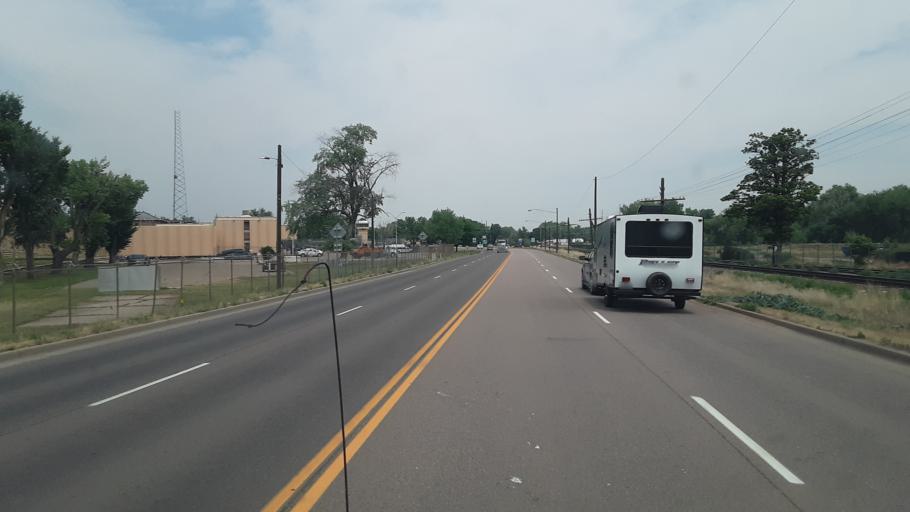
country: US
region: Colorado
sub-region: Fremont County
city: Canon City
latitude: 38.4353
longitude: -105.2510
